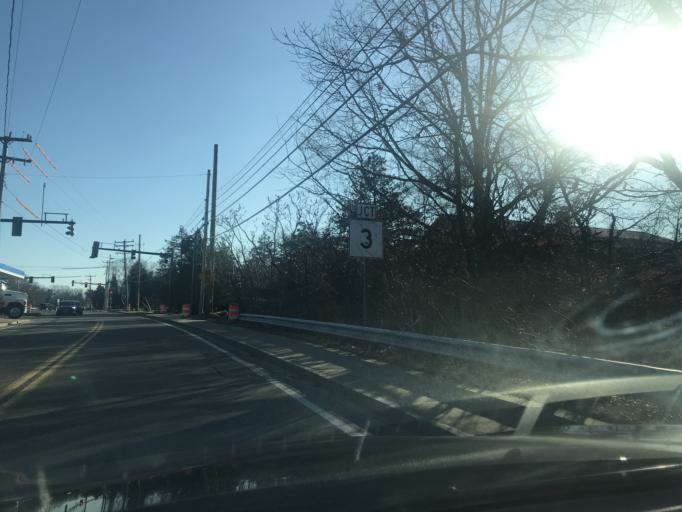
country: US
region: Massachusetts
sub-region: Plymouth County
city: Plymouth
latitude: 41.9393
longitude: -70.6572
